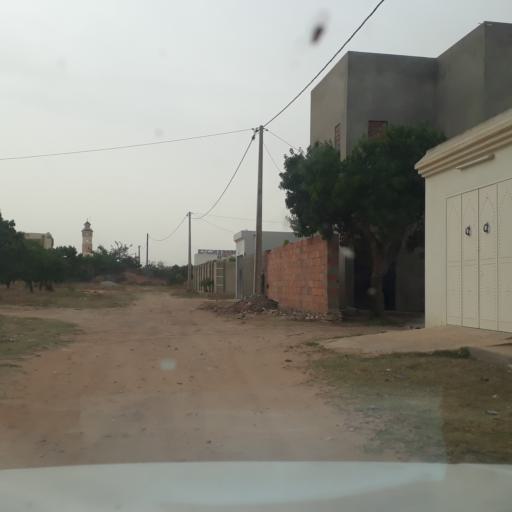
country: TN
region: Safaqis
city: Al Qarmadah
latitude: 34.8239
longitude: 10.7748
